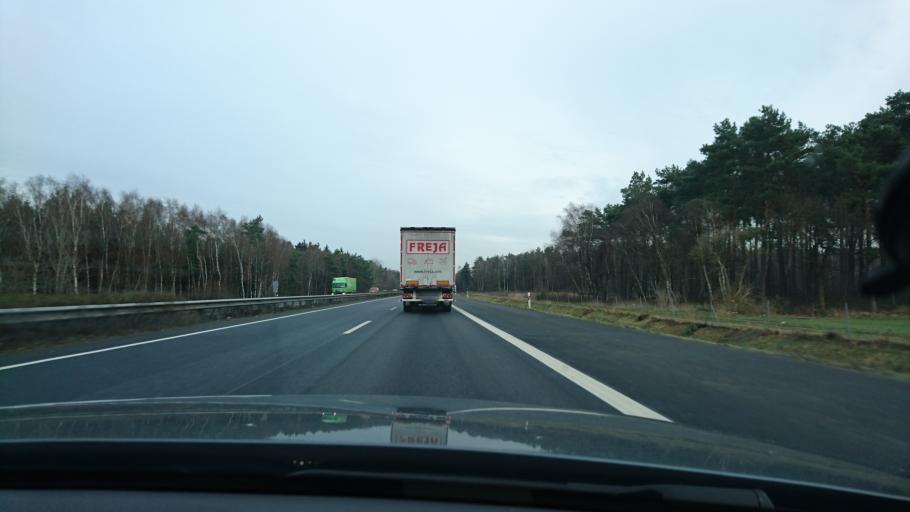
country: DE
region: Lower Saxony
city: Rieste
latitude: 52.4279
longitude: 8.0319
